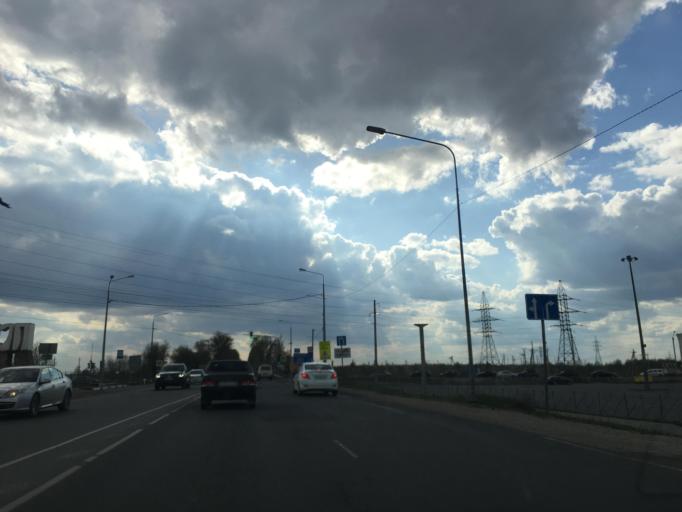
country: RU
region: Pskov
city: Pskov
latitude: 57.8047
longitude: 28.2594
